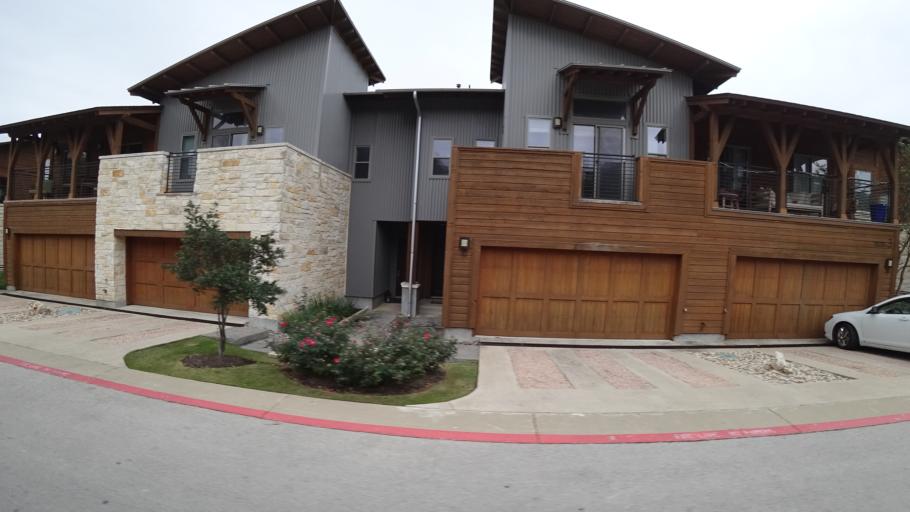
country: US
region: Texas
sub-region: Williamson County
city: Jollyville
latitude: 30.3801
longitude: -97.8062
